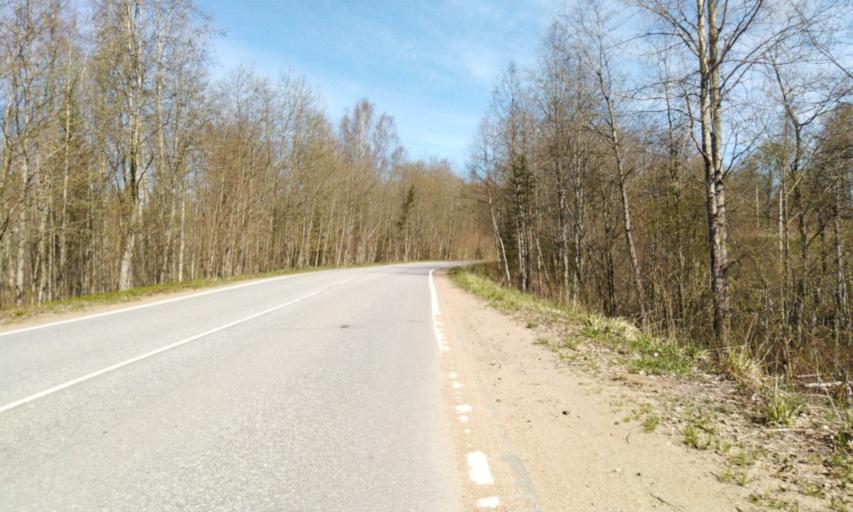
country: RU
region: Leningrad
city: Garbolovo
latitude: 60.4164
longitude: 30.4579
